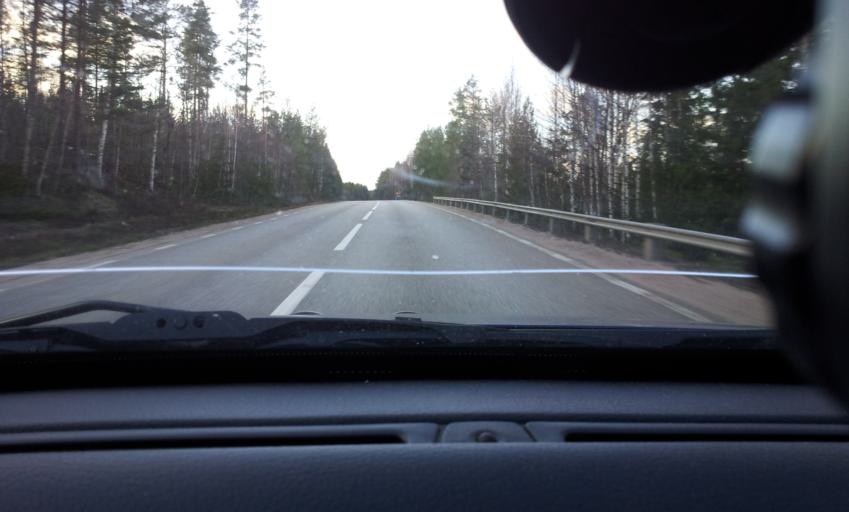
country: SE
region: Vaesternorrland
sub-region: Ange Kommun
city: Ange
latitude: 62.0785
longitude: 15.0999
